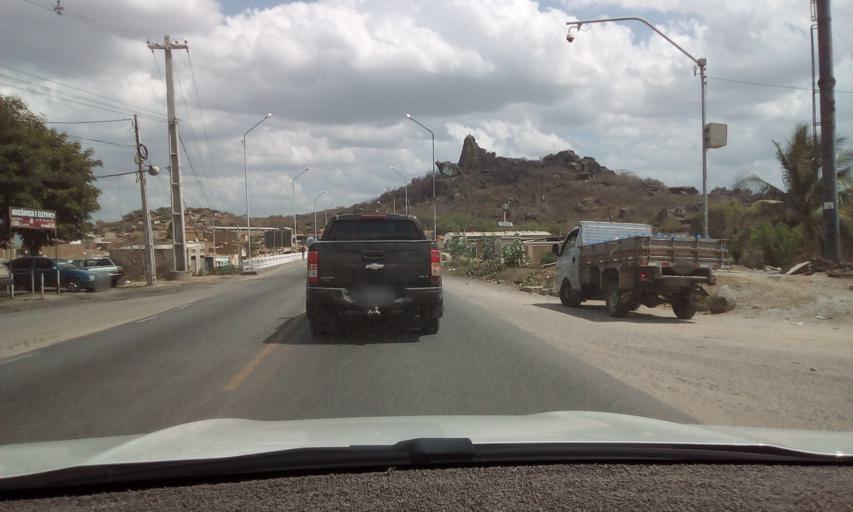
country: BR
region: Pernambuco
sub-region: Toritama
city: Toritama
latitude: -8.0109
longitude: -36.0575
